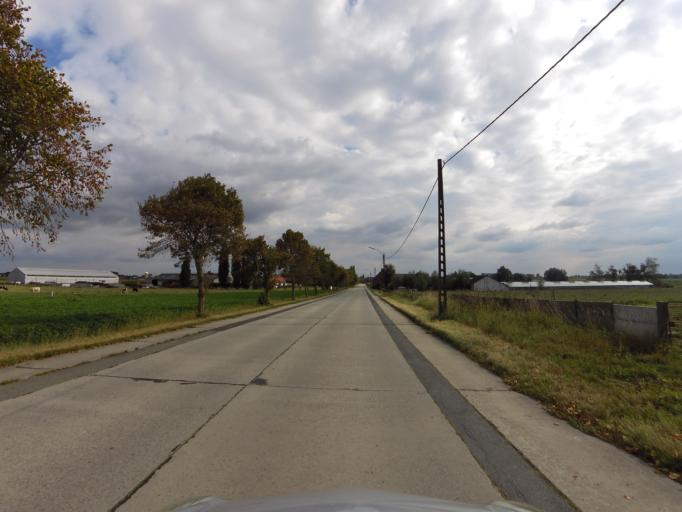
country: BE
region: Flanders
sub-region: Provincie West-Vlaanderen
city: Pittem
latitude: 51.0114
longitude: 3.2864
